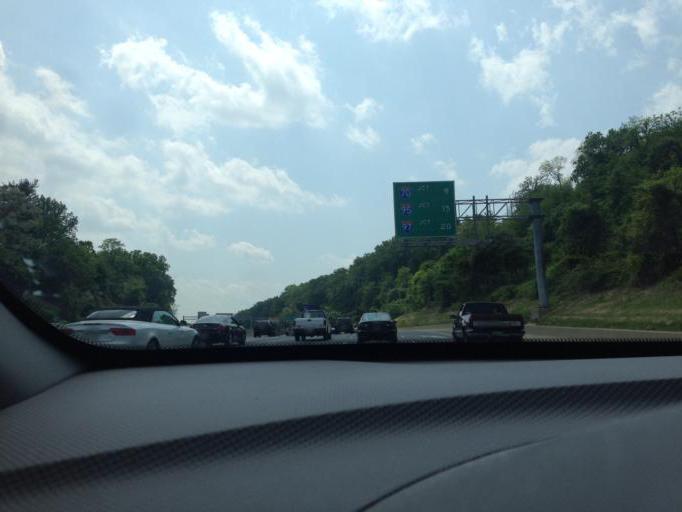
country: US
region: Maryland
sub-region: Baltimore County
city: Mays Chapel
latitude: 39.4055
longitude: -76.6726
